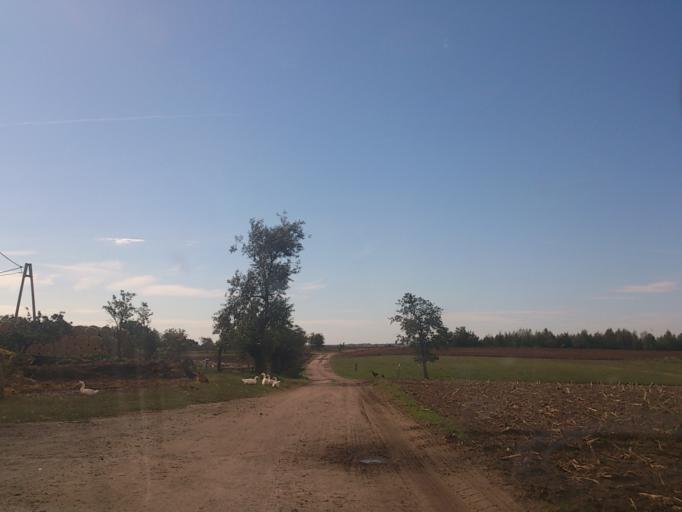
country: PL
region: Kujawsko-Pomorskie
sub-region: Powiat golubsko-dobrzynski
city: Radomin
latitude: 53.1217
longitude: 19.1353
